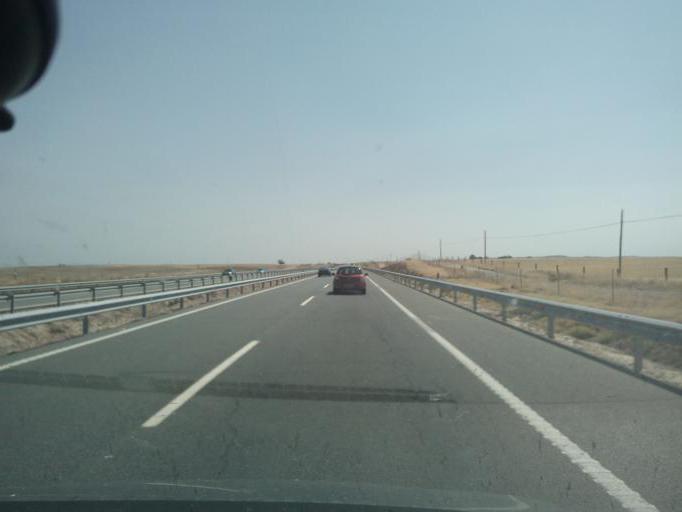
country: ES
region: Extremadura
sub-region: Provincia de Caceres
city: Berrocalejo
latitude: 39.8921
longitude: -5.3877
